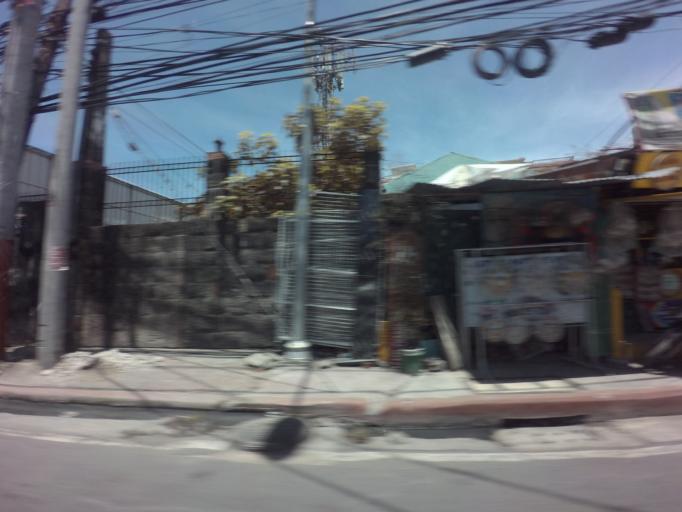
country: PH
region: Calabarzon
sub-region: Province of Rizal
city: Las Pinas
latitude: 14.4774
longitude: 120.9777
